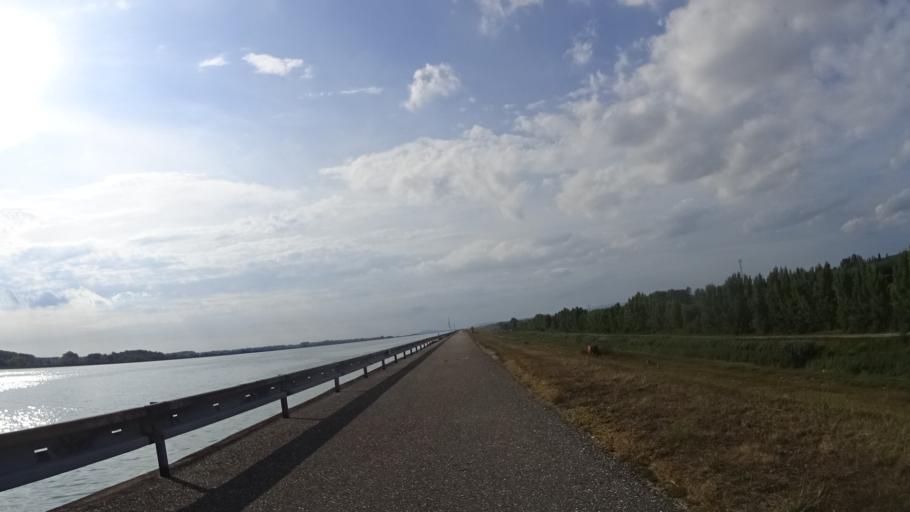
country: HU
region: Gyor-Moson-Sopron
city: Asvanyraro
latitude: 47.9426
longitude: 17.4520
